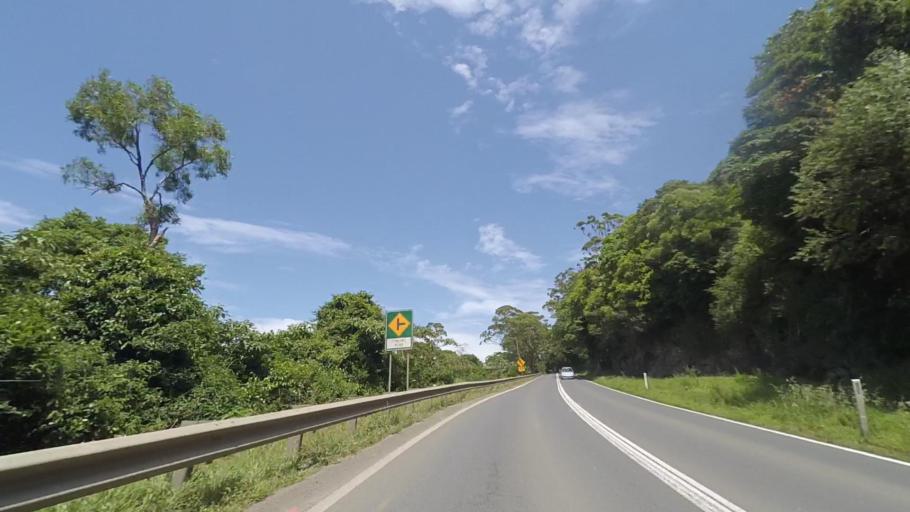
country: AU
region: New South Wales
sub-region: Shoalhaven Shire
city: Berry
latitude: -34.7498
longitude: 150.7500
